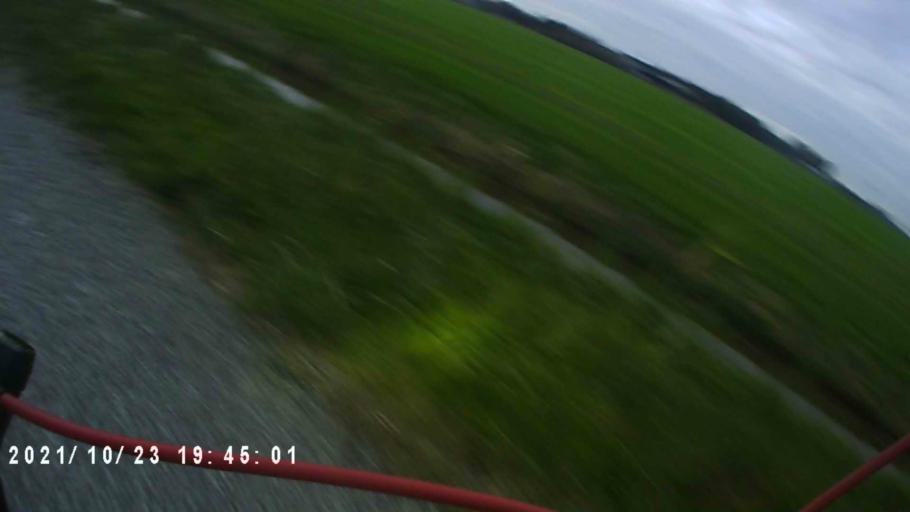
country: NL
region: Friesland
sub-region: Sudwest Fryslan
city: Makkum
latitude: 53.0811
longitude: 5.4305
